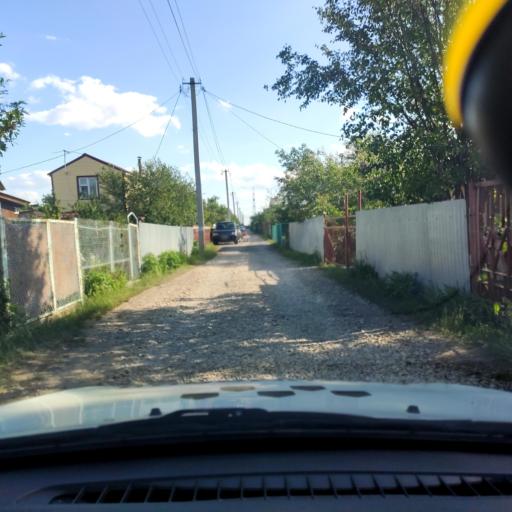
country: RU
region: Samara
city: Tol'yatti
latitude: 53.5947
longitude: 49.2939
